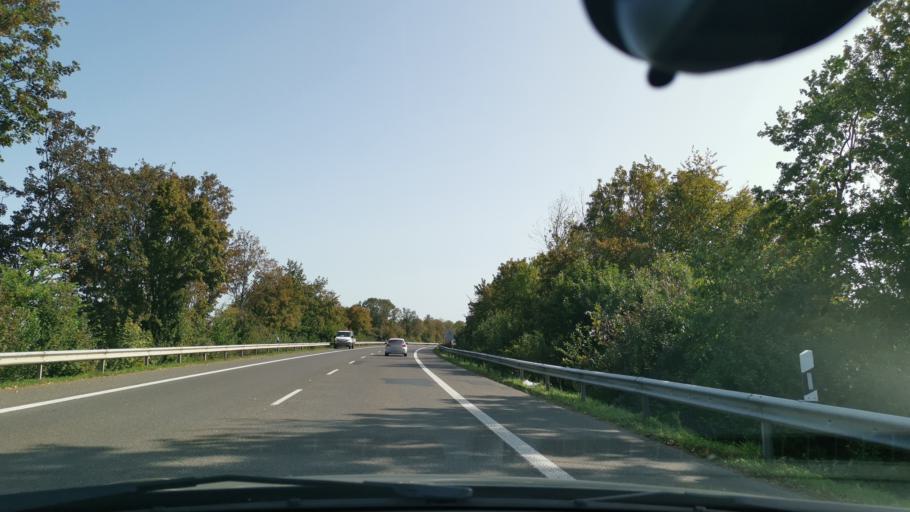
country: DE
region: North Rhine-Westphalia
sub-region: Regierungsbezirk Dusseldorf
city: Neubrueck
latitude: 51.1360
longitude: 6.6271
